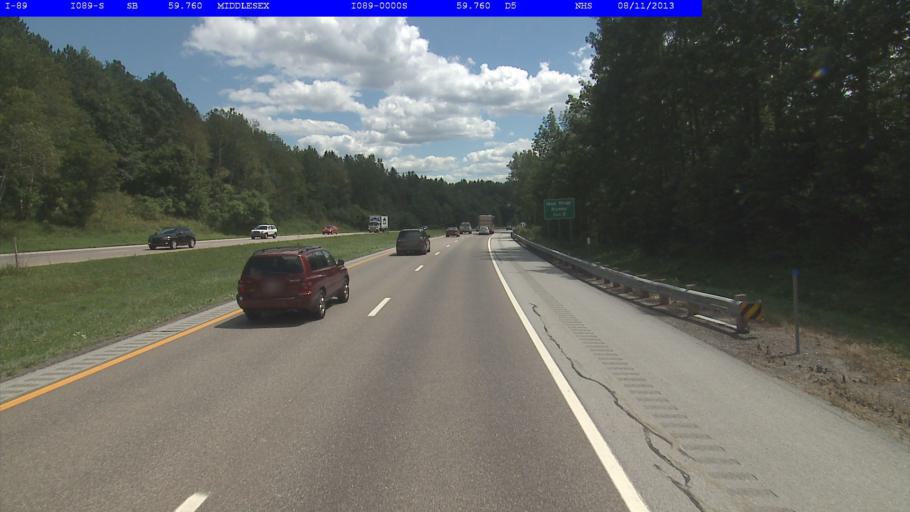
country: US
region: Vermont
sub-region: Washington County
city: Waterbury
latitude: 44.3115
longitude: -72.6948
